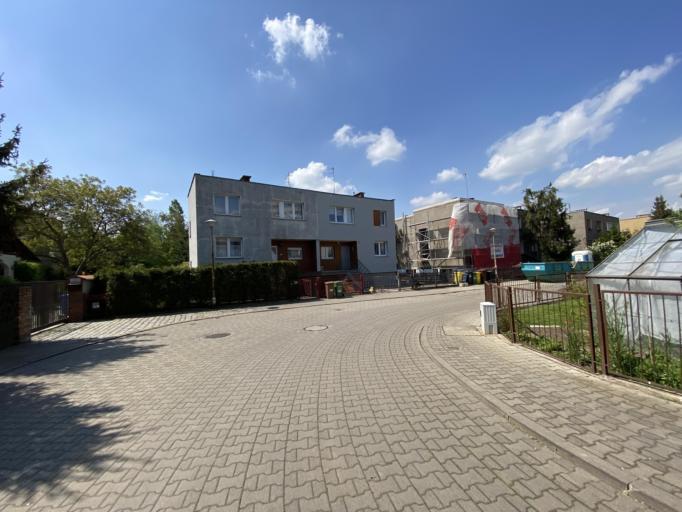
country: PL
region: Lower Silesian Voivodeship
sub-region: Powiat wroclawski
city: Wroclaw
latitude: 51.1356
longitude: 17.0237
